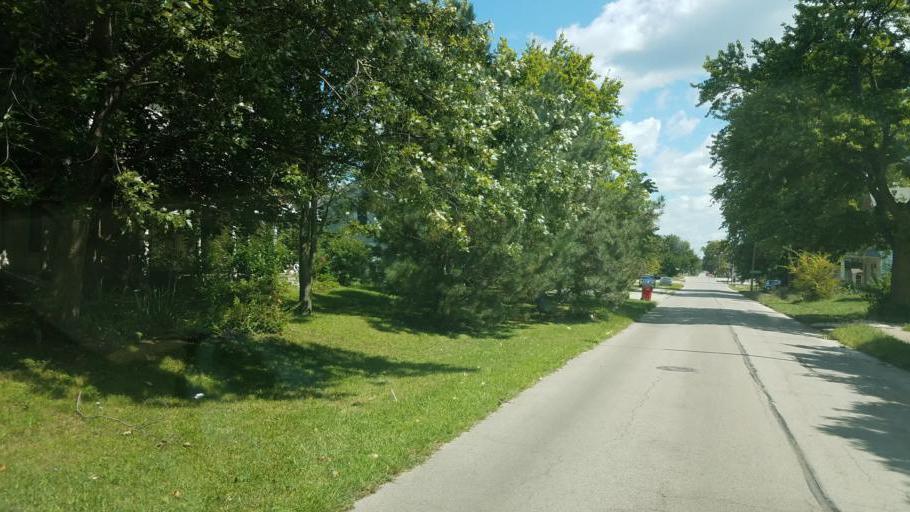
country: US
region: Ohio
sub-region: Seneca County
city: Fostoria
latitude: 41.1599
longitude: -83.4123
